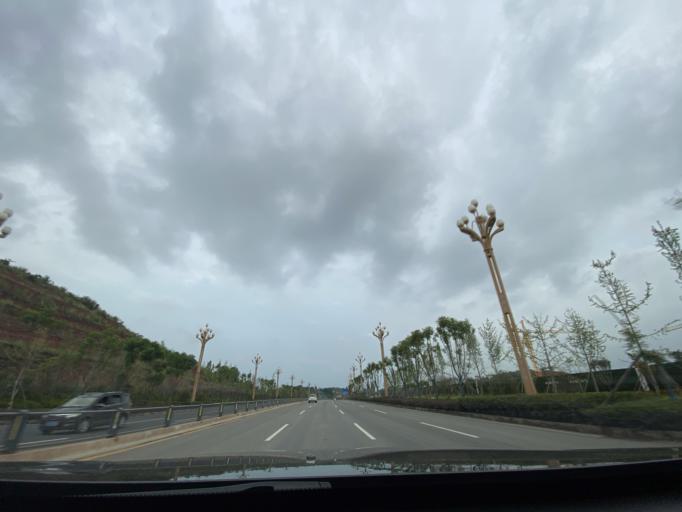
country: CN
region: Sichuan
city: Jiancheng
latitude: 30.4839
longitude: 104.4822
